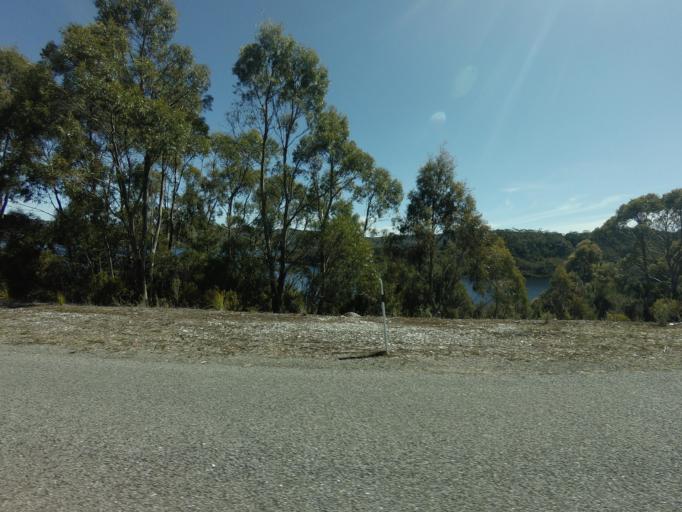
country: AU
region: Tasmania
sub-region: Huon Valley
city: Geeveston
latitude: -42.8282
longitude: 146.1260
